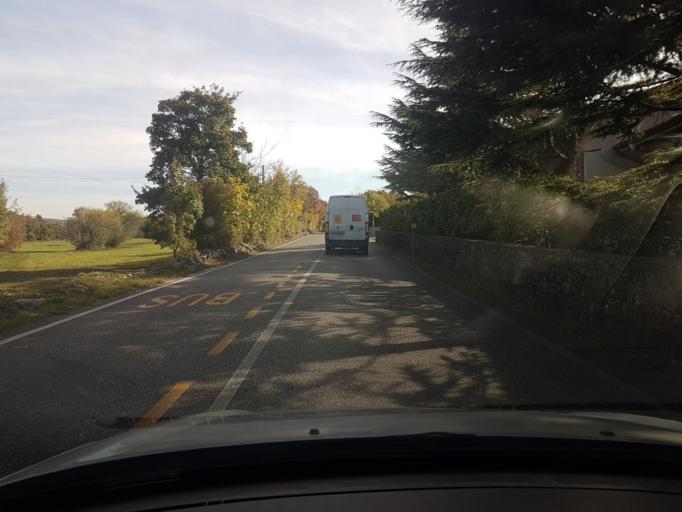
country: IT
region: Friuli Venezia Giulia
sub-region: Provincia di Trieste
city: Santa Croce
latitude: 45.7323
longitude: 13.7005
